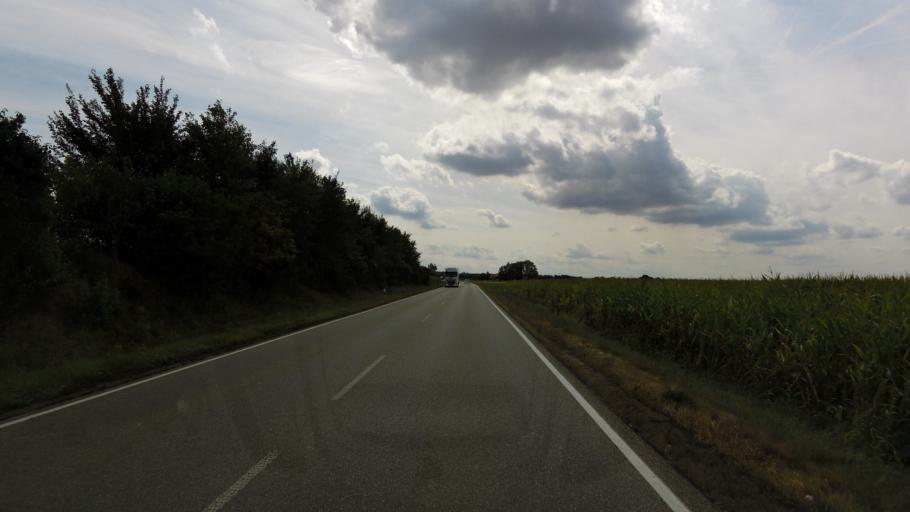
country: DE
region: Bavaria
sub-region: Upper Bavaria
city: Unterneukirchen
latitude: 48.1627
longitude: 12.6113
